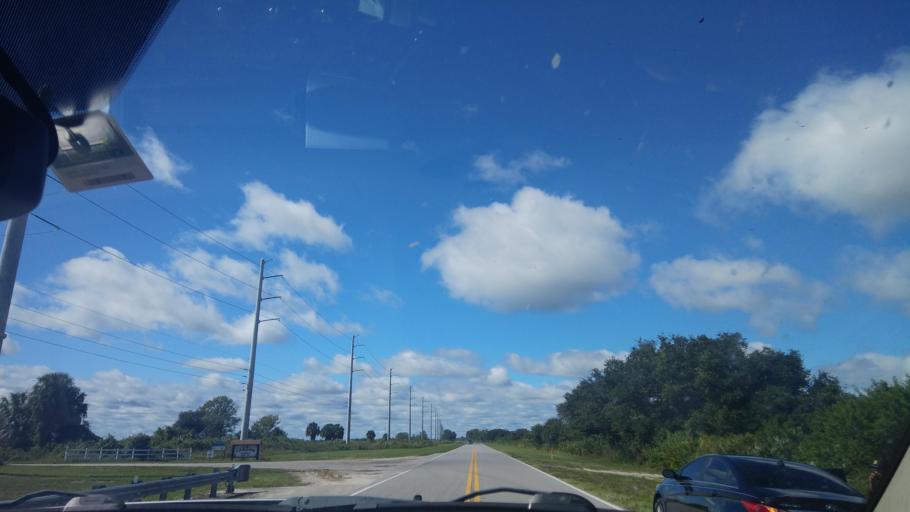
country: US
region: Florida
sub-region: Okeechobee County
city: Cypress Quarters
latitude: 27.4492
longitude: -80.7758
